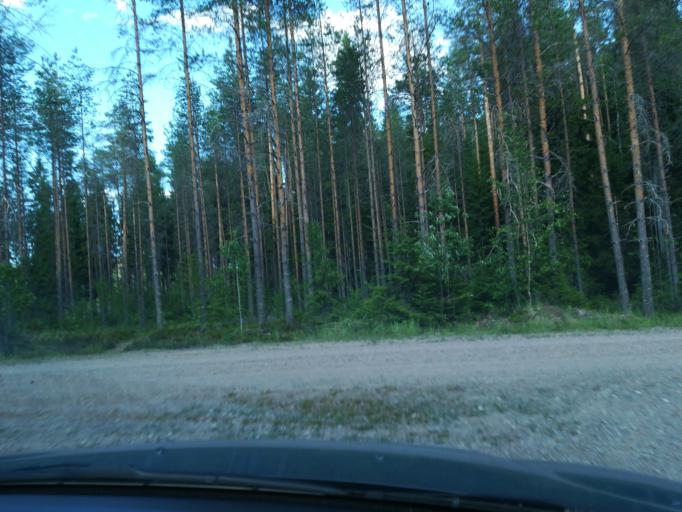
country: FI
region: South Karelia
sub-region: Imatra
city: Ruokolahti
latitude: 61.5386
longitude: 28.8187
